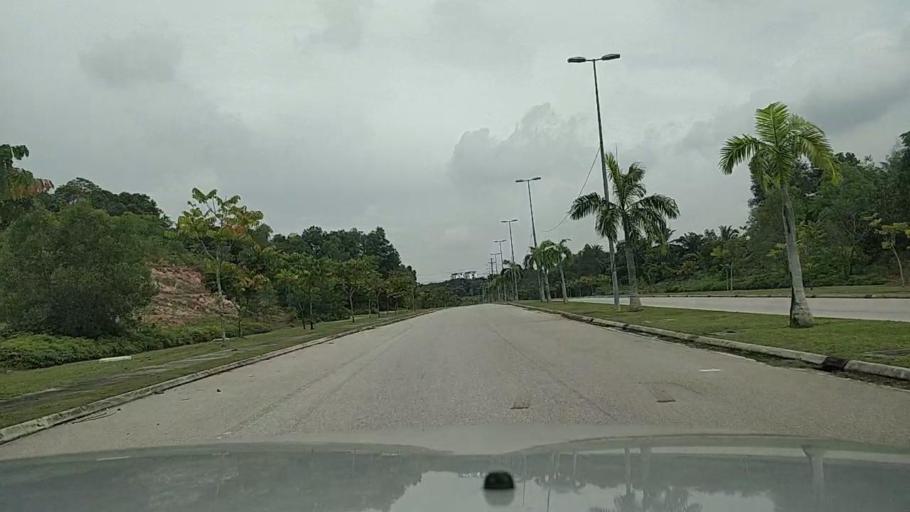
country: MY
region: Putrajaya
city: Putrajaya
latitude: 2.9001
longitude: 101.6473
